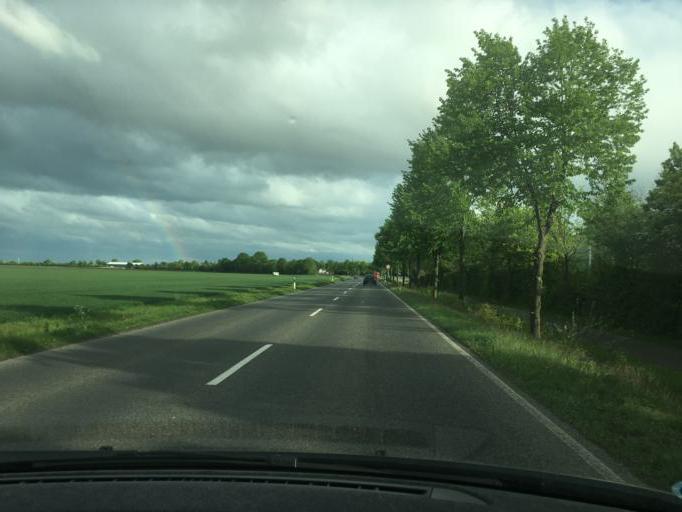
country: DE
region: North Rhine-Westphalia
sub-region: Regierungsbezirk Koln
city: Merzenich
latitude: 50.8198
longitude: 6.5460
